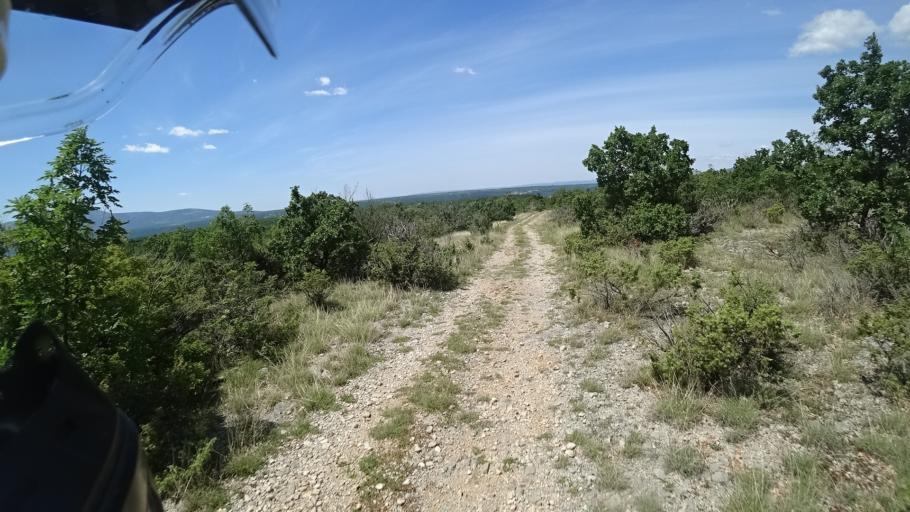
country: HR
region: Sibensko-Kniniska
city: Knin
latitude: 44.0328
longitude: 16.2452
